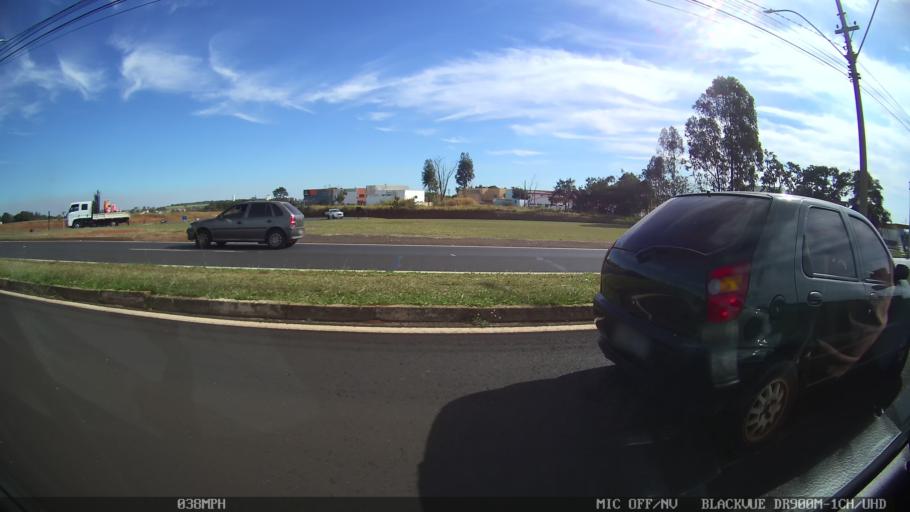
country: BR
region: Sao Paulo
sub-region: Araraquara
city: Araraquara
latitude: -21.8113
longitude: -48.1587
